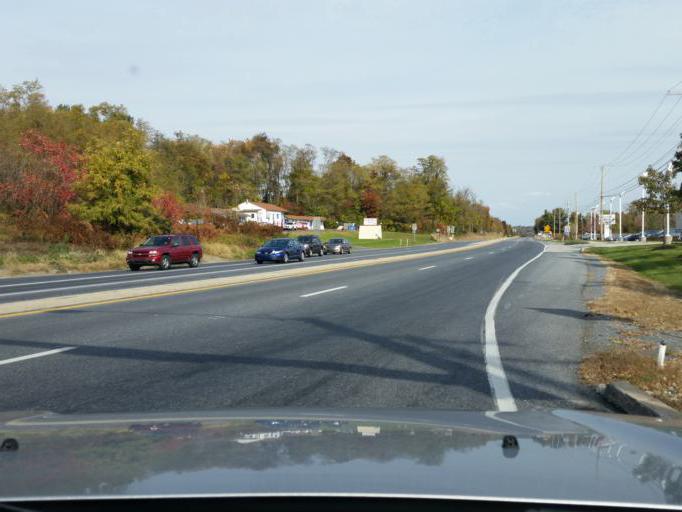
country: US
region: Pennsylvania
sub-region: Dauphin County
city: Skyline View
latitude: 40.3388
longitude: -76.7113
